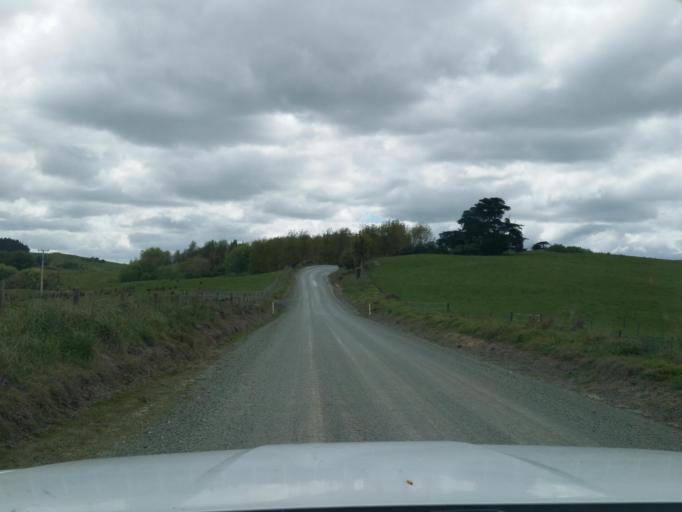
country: NZ
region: Auckland
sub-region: Auckland
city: Wellsford
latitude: -36.2632
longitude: 174.3685
